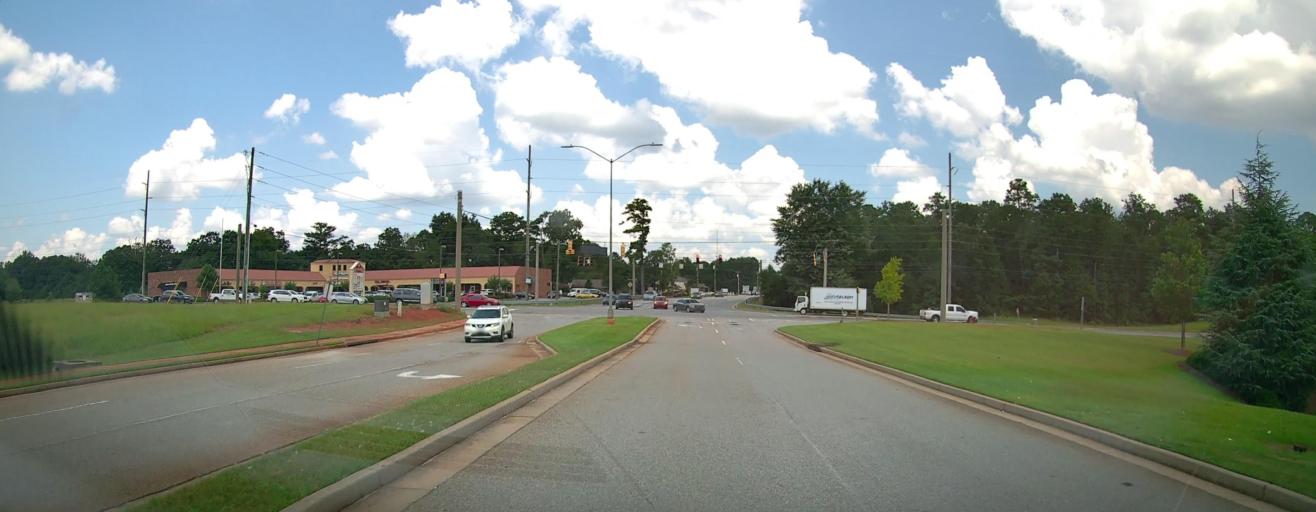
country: US
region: Georgia
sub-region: Houston County
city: Centerville
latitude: 32.5926
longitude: -83.6649
